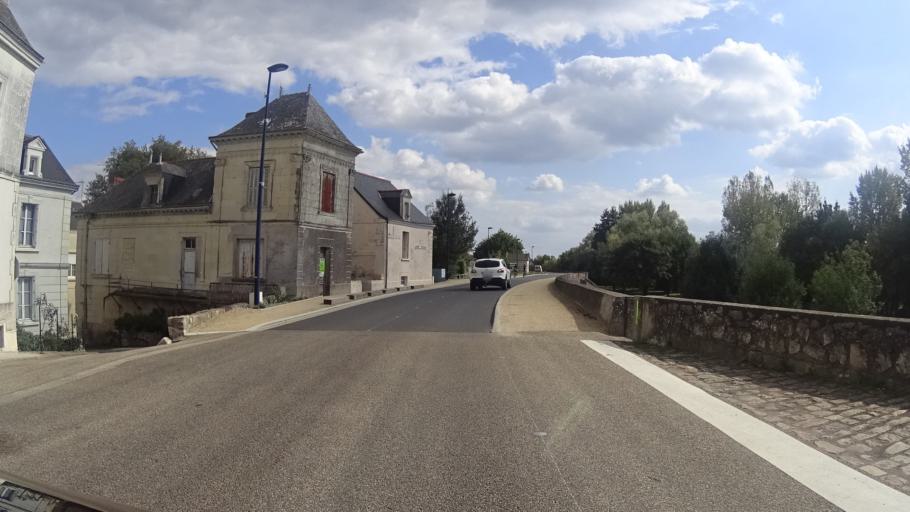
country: FR
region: Pays de la Loire
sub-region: Departement de Maine-et-Loire
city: Saint-Clement-des-Levees
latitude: 47.3300
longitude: -0.1834
